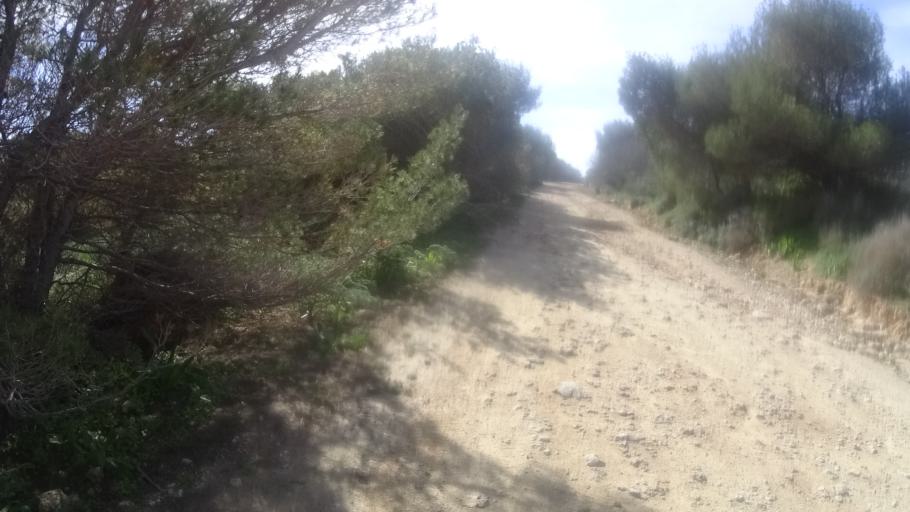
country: MT
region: Il-Qala
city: Qala
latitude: 36.0143
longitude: 14.3345
